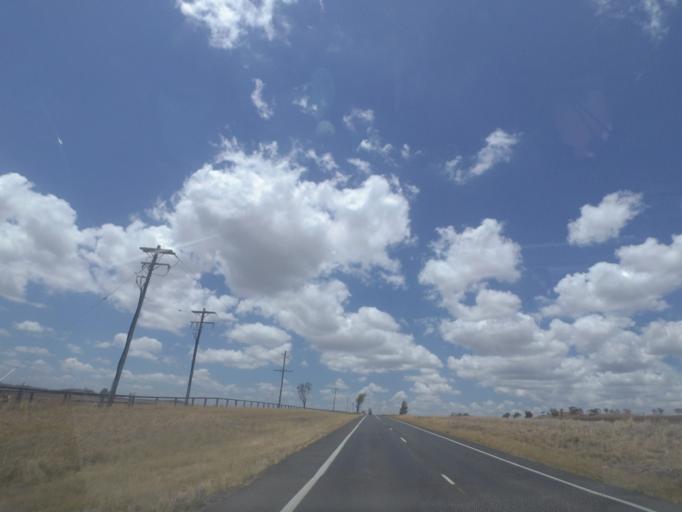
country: AU
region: Queensland
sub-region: Toowoomba
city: Top Camp
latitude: -27.7444
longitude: 151.9266
